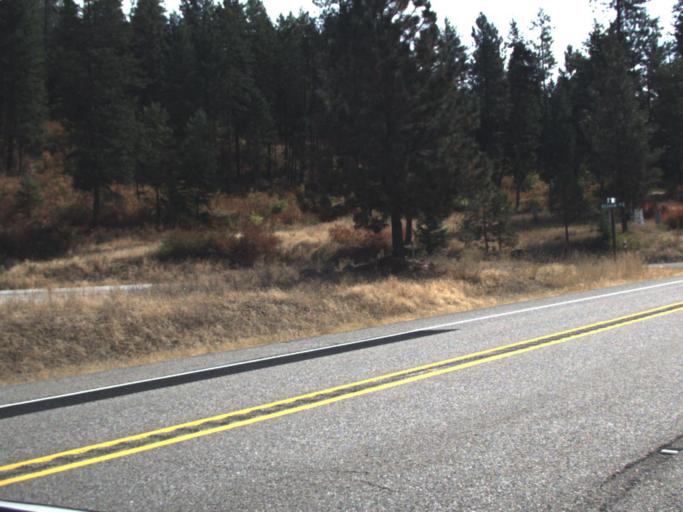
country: US
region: Washington
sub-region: Stevens County
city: Chewelah
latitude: 48.1885
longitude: -117.7005
